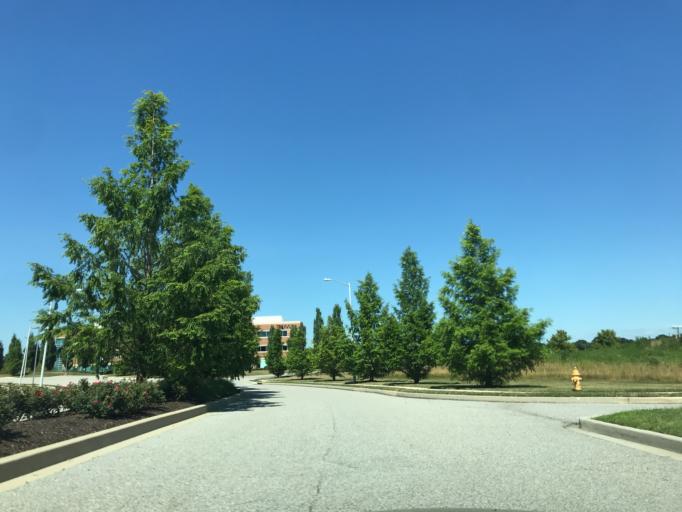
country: US
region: Maryland
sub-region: Harford County
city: Aberdeen
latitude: 39.5018
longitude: -76.1492
